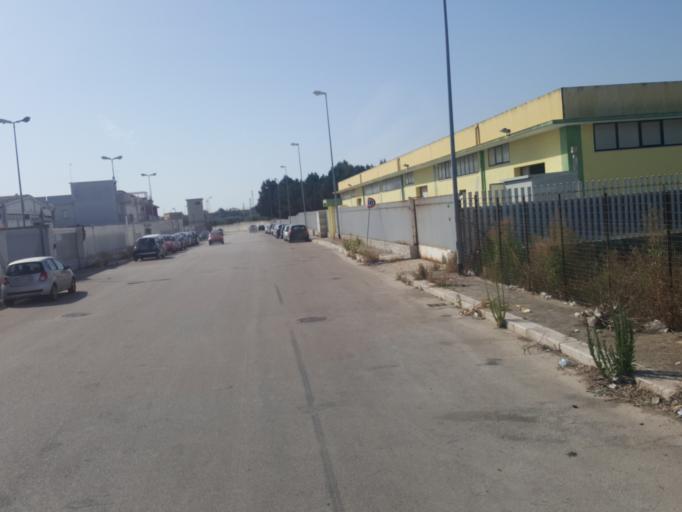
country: IT
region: Apulia
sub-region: Provincia di Barletta - Andria - Trani
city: Barletta
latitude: 41.3089
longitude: 16.3049
